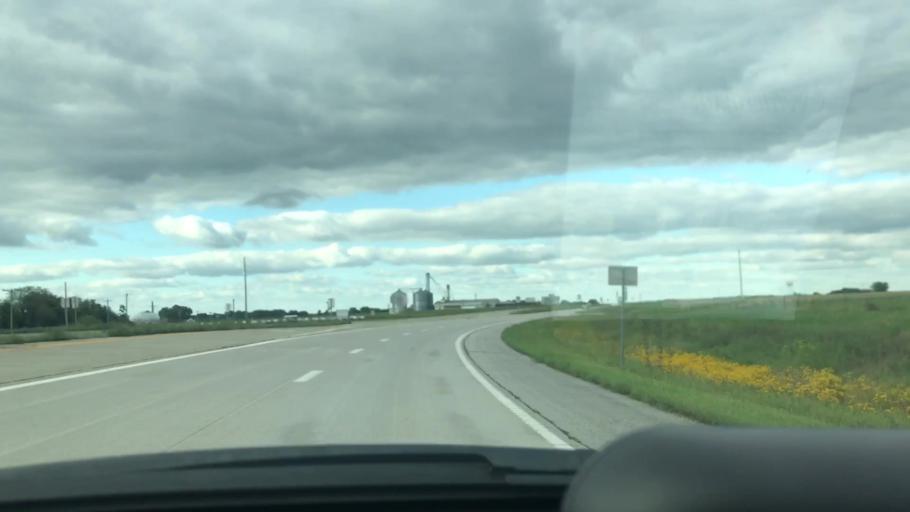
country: US
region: Missouri
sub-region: Benton County
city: Lincoln
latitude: 38.3752
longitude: -93.3384
